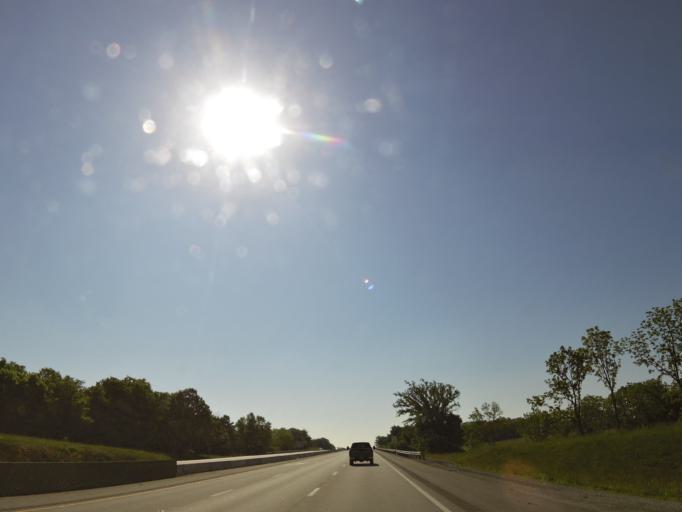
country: US
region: Kentucky
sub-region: Shelby County
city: Shelbyville
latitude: 38.1900
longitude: -85.2642
